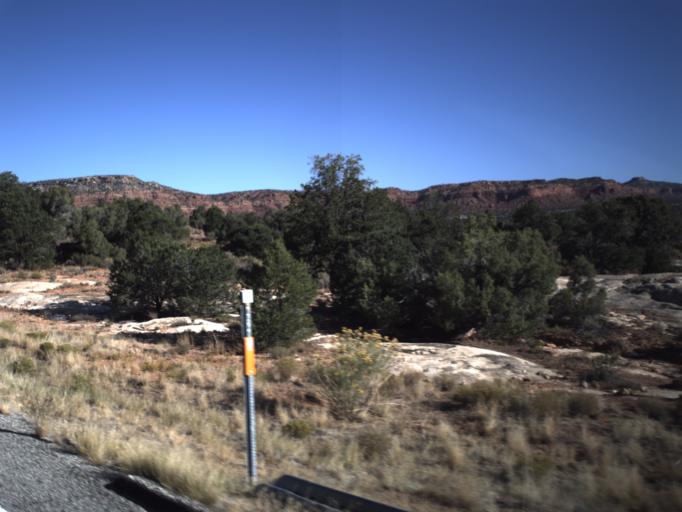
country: US
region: Utah
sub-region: San Juan County
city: Blanding
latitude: 37.6430
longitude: -110.1115
